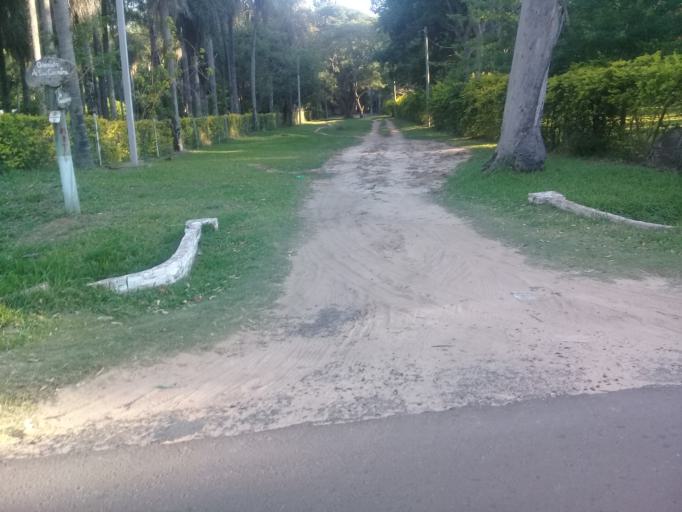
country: AR
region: Corrientes
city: San Luis del Palmar
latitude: -27.4597
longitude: -58.6632
